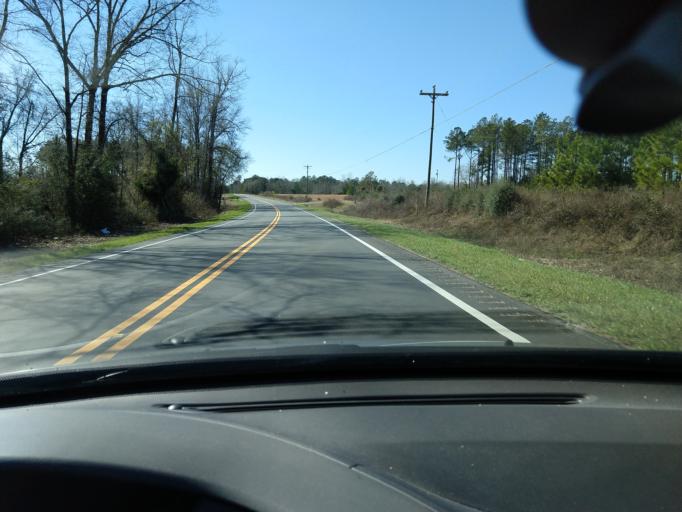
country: US
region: Alabama
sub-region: Covington County
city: Andalusia
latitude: 31.2049
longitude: -86.5528
